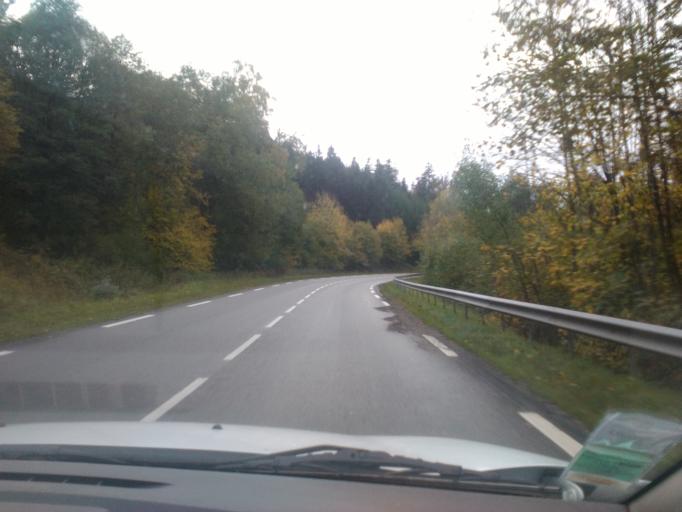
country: FR
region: Lorraine
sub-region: Departement des Vosges
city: Corcieux
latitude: 48.1390
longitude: 6.9167
